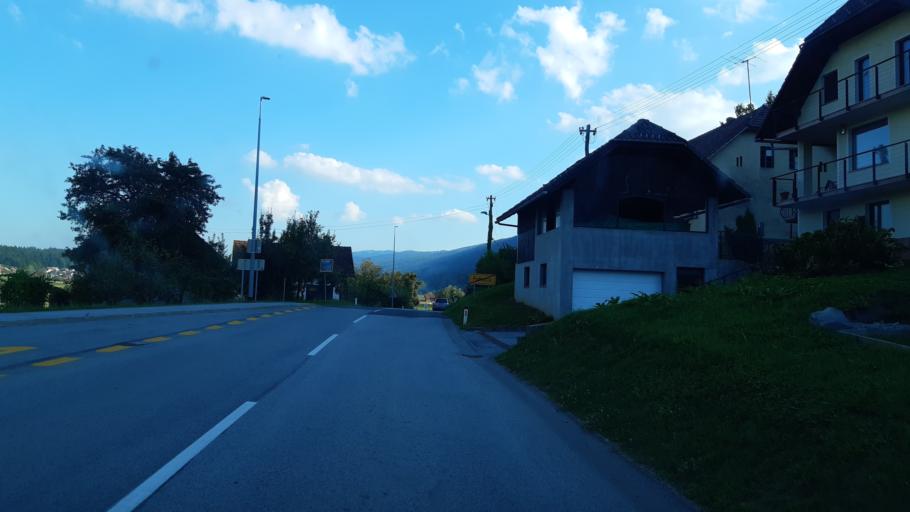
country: SI
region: Dolenjske Toplice
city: Dolenjske Toplice
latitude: 45.7586
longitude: 15.0328
